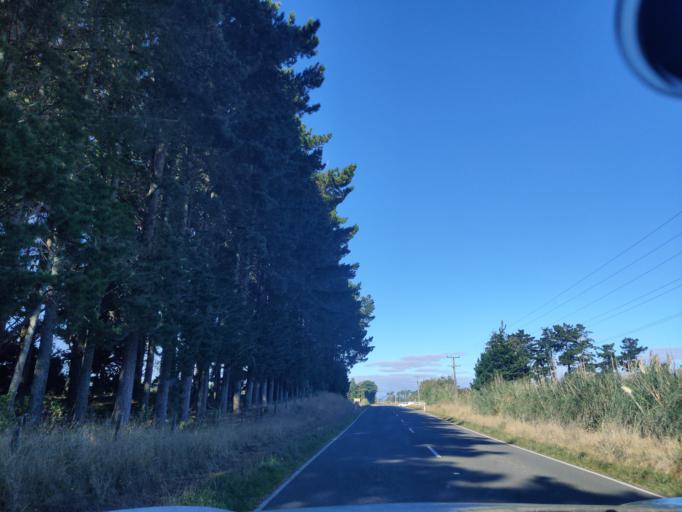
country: NZ
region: Manawatu-Wanganui
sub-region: Horowhenua District
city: Foxton
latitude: -40.3868
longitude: 175.2916
